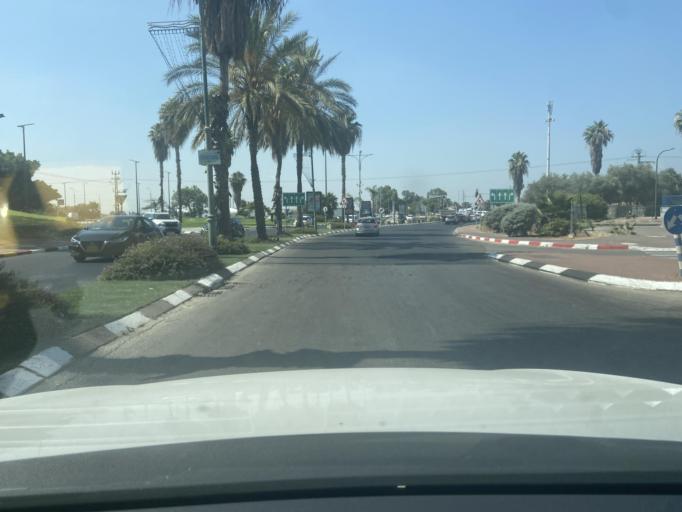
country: IL
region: Central District
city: Yehud
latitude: 32.0291
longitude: 34.8808
